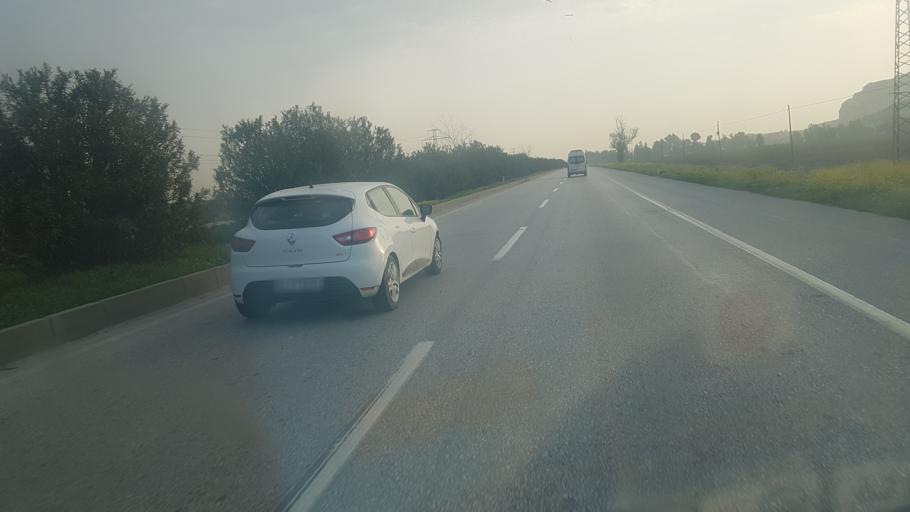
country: TR
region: Adana
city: Yakapinar
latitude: 37.0125
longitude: 35.7083
